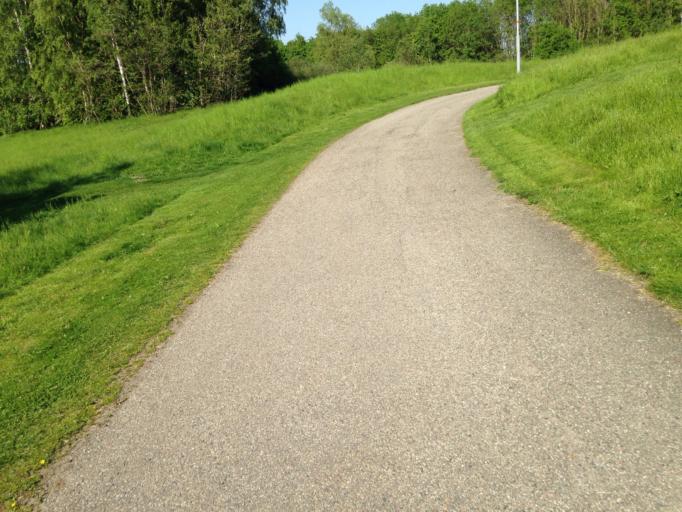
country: SE
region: Skane
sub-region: Burlovs Kommun
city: Arloev
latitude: 55.5995
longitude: 13.0699
